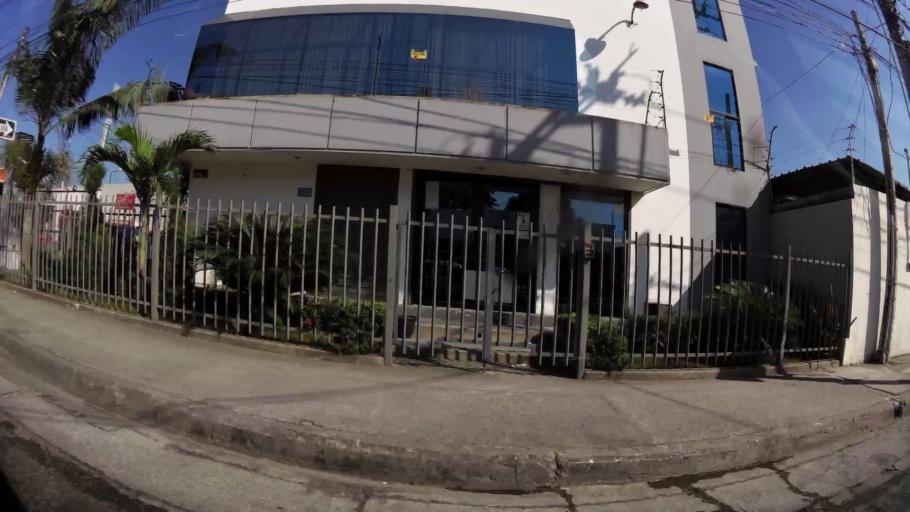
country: EC
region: Guayas
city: Eloy Alfaro
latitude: -2.1488
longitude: -79.9007
